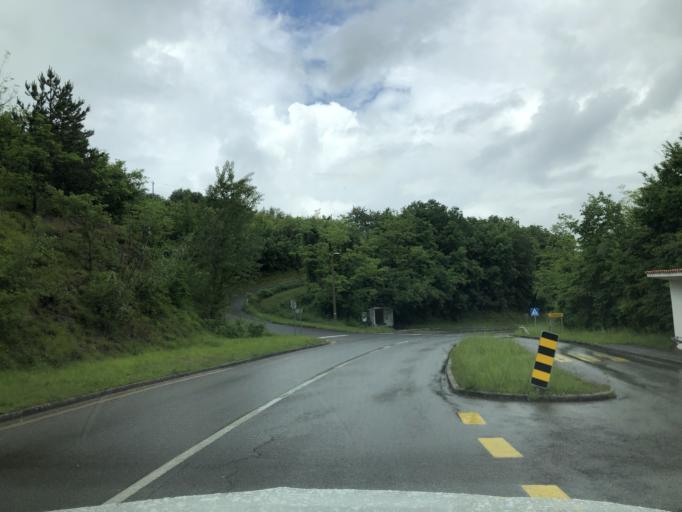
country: SI
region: Koper-Capodistria
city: Prade
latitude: 45.5029
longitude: 13.7725
